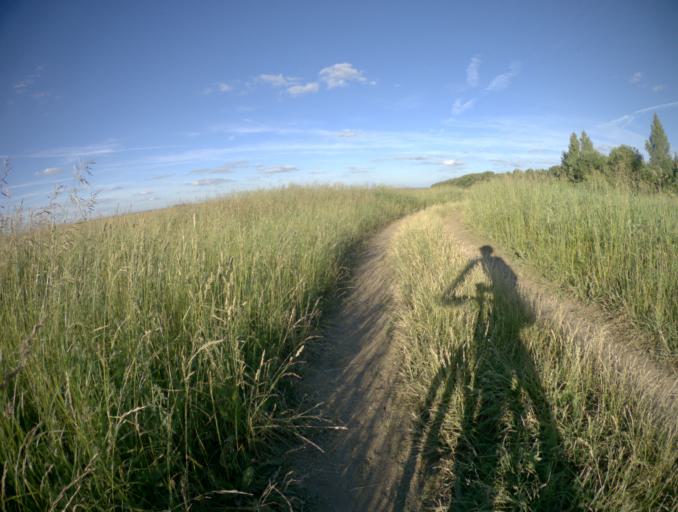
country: RU
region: Vladimir
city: Bogolyubovo
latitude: 56.1837
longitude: 40.4666
